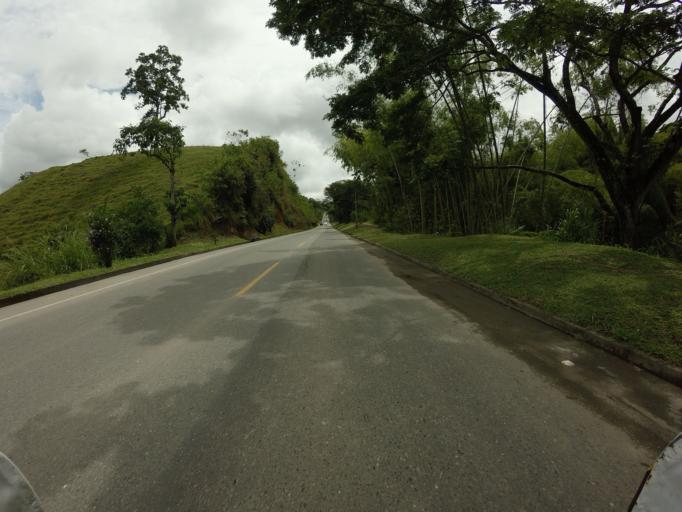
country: CO
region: Quindio
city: Quimbaya
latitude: 4.6343
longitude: -75.7731
